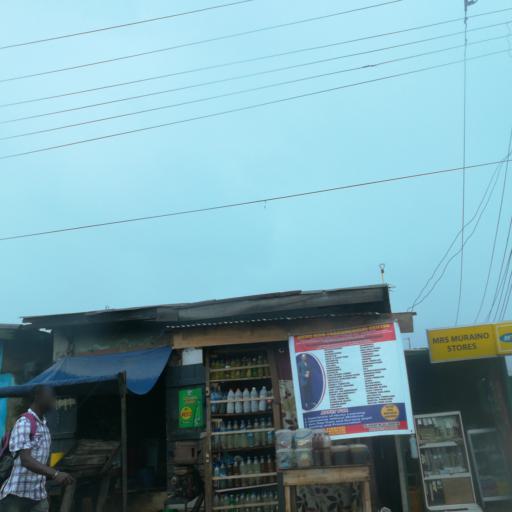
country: NG
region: Lagos
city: Oshodi
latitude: 6.5566
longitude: 3.3404
